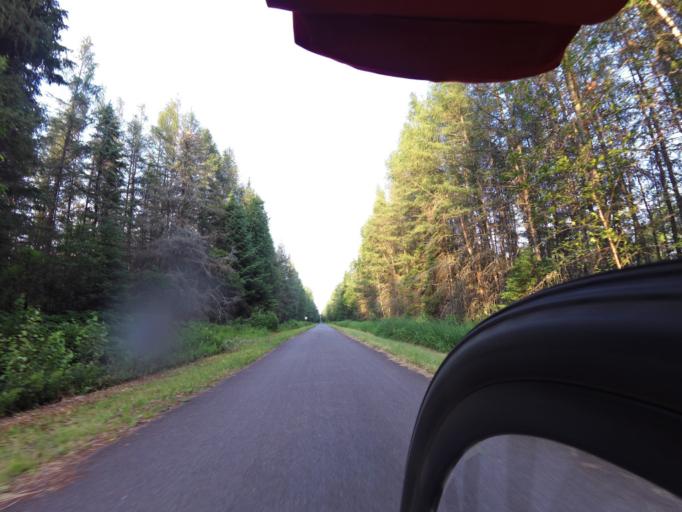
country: CA
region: Quebec
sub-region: Laurentides
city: Riviere-Rouge
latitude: 46.3938
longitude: -75.0222
